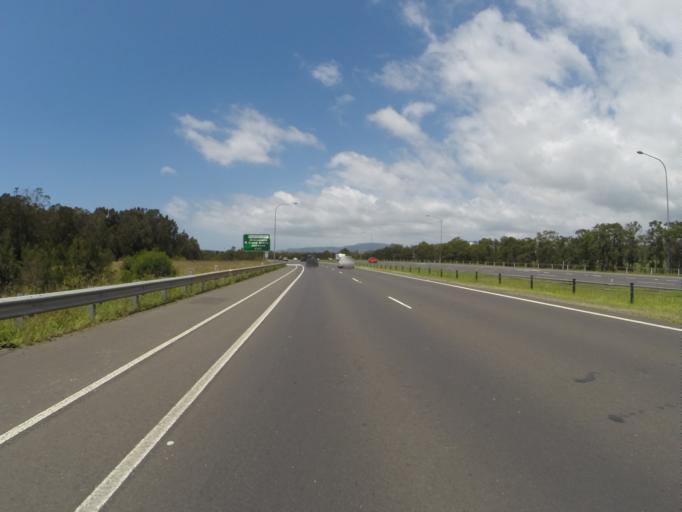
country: AU
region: New South Wales
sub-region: Shellharbour
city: Croom
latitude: -34.6112
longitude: 150.8375
